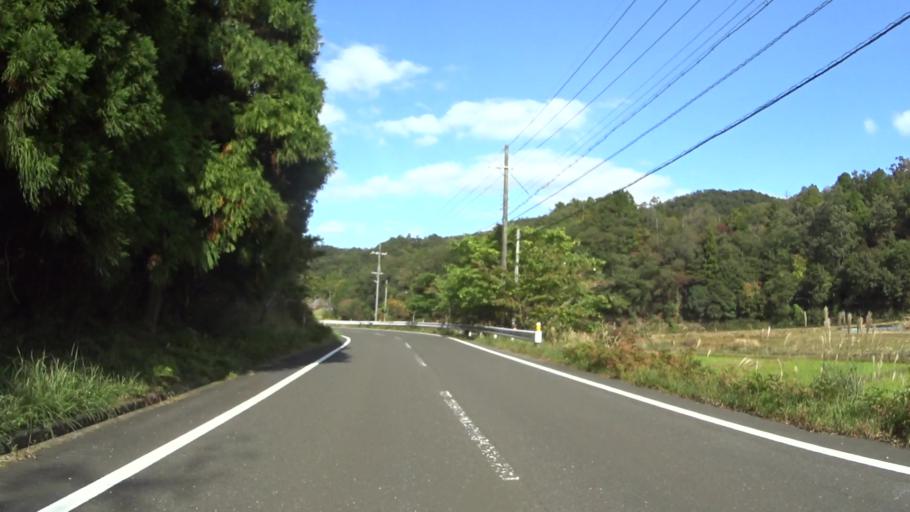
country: JP
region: Hyogo
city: Toyooka
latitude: 35.5580
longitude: 134.9795
